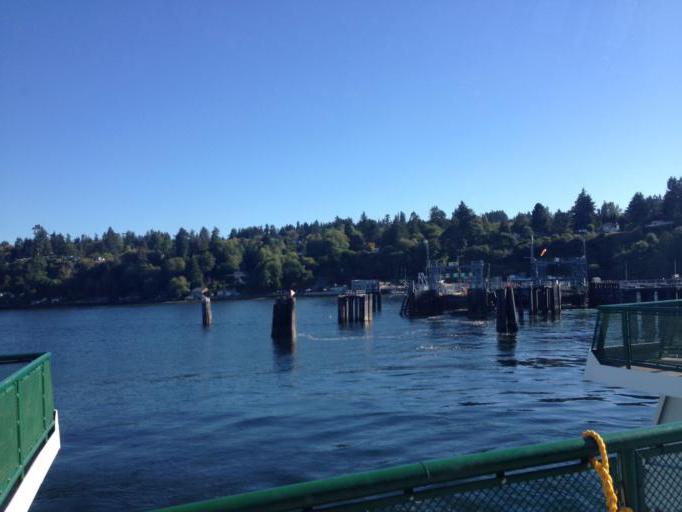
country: US
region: Washington
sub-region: Kitsap County
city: Southworth
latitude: 47.5121
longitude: -122.4627
